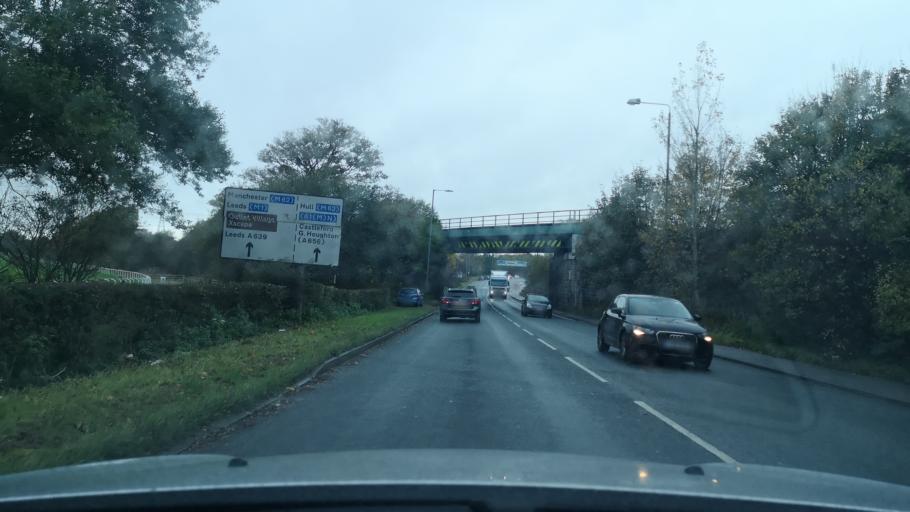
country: GB
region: England
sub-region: City and Borough of Wakefield
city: Pontefract
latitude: 53.7041
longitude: -1.3282
